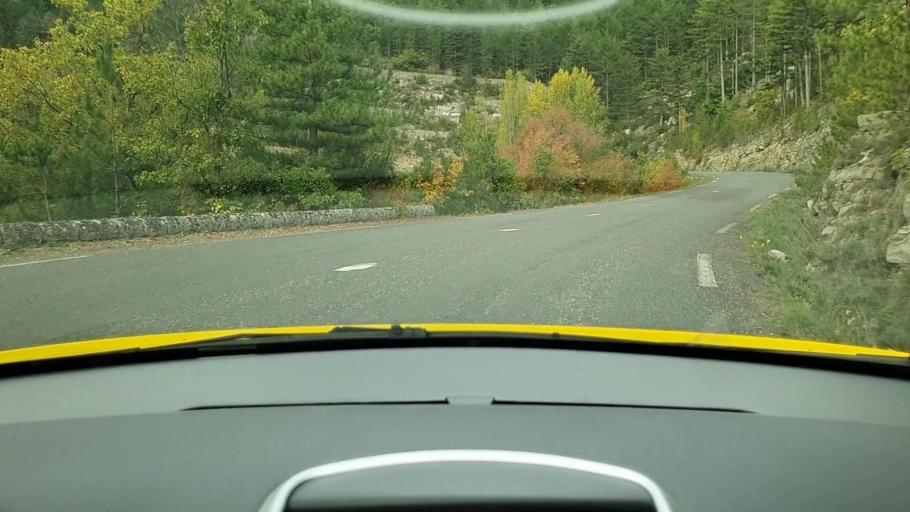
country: FR
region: Languedoc-Roussillon
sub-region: Departement de la Lozere
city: Meyrueis
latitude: 44.0785
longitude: 3.3719
